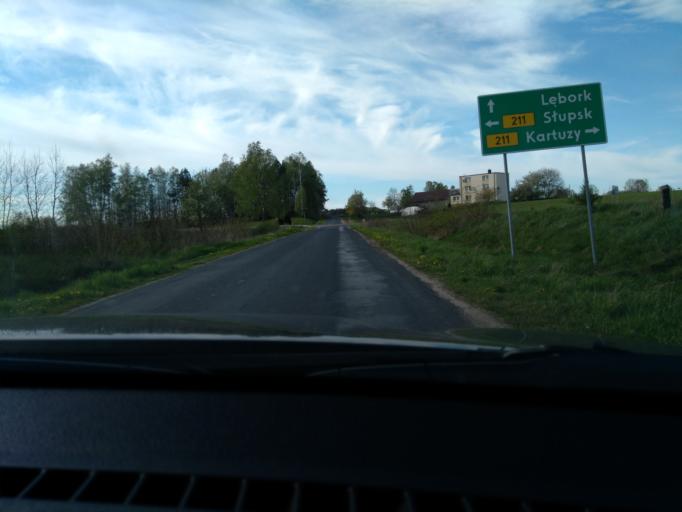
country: PL
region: Pomeranian Voivodeship
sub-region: Powiat leborski
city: Cewice
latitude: 54.3407
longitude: 17.6826
